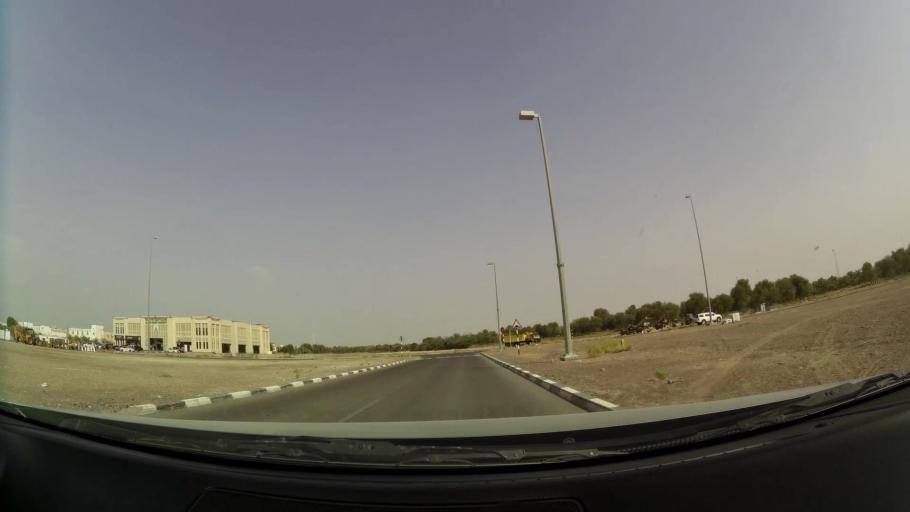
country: AE
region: Abu Dhabi
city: Al Ain
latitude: 24.2041
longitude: 55.5829
